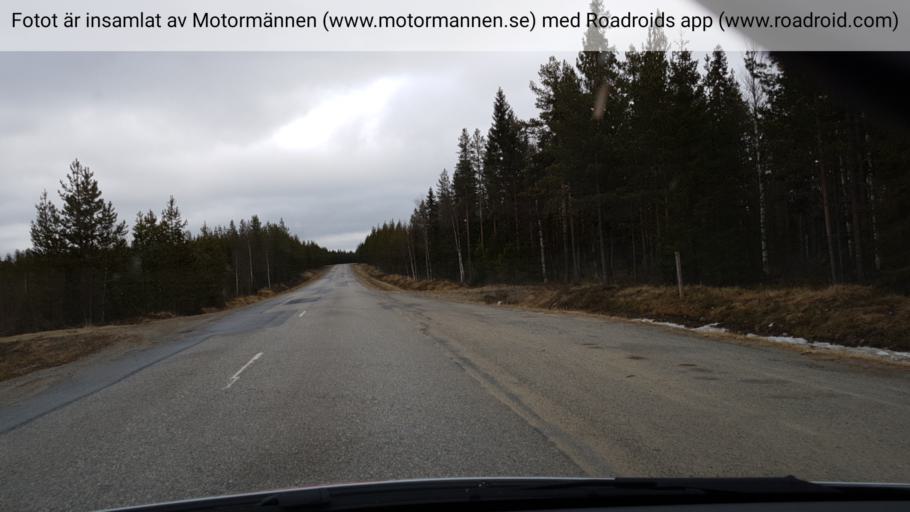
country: SE
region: Vaesterbotten
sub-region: Lycksele Kommun
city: Lycksele
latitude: 64.0590
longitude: 18.4098
